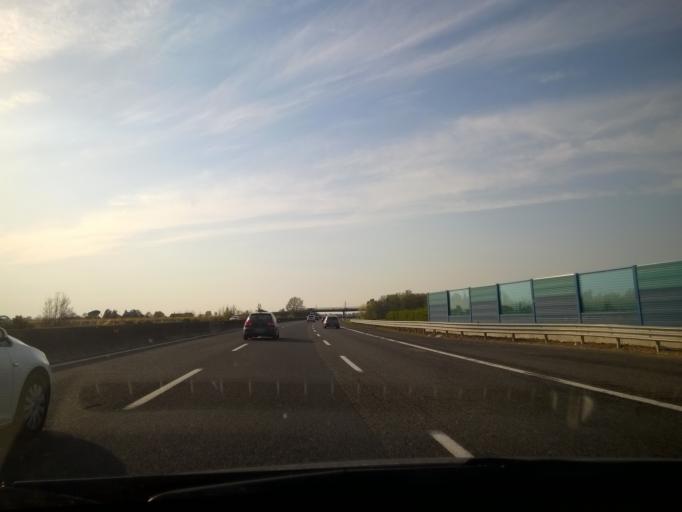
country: IT
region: Emilia-Romagna
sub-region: Forli-Cesena
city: Forli
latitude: 44.2725
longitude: 12.0344
